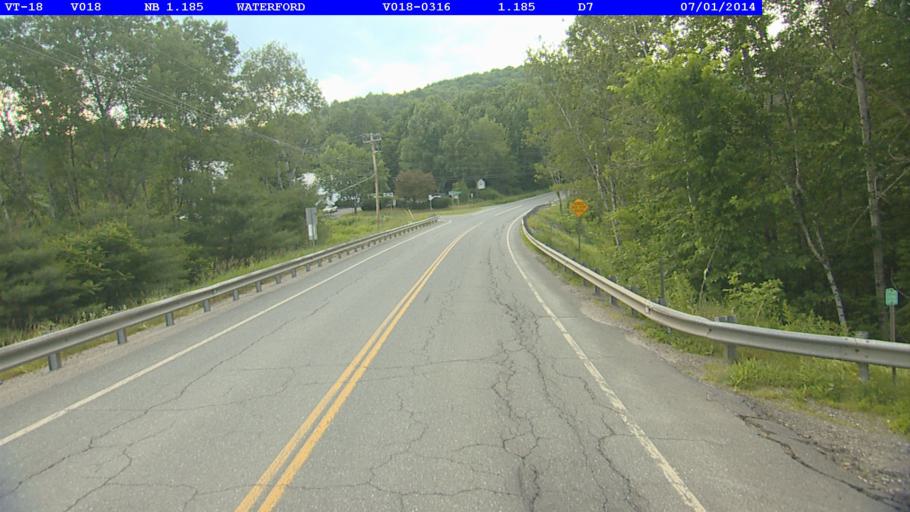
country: US
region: Vermont
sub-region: Caledonia County
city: Saint Johnsbury
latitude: 44.3545
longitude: -71.9056
